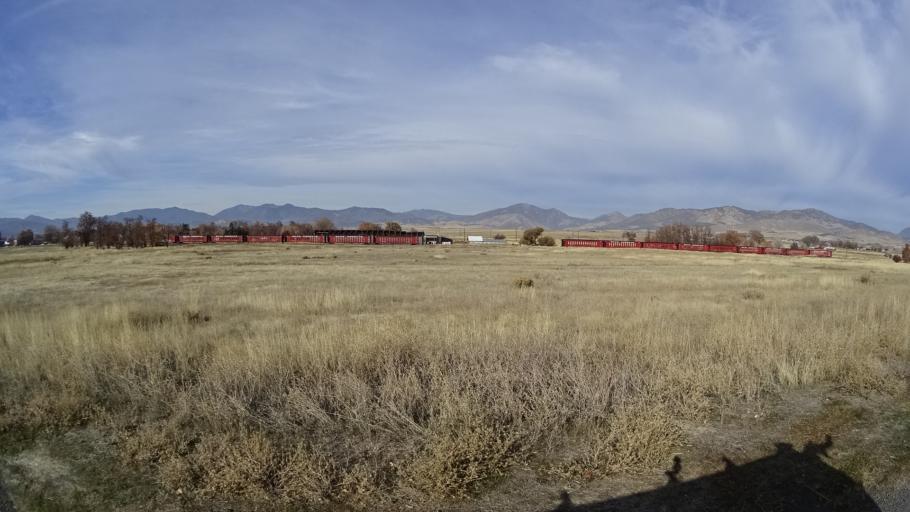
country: US
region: California
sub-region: Siskiyou County
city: Montague
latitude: 41.7313
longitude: -122.5217
